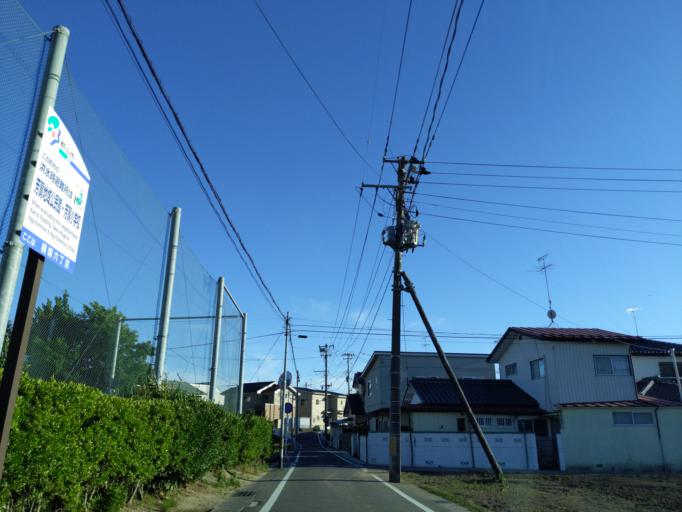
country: JP
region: Fukushima
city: Koriyama
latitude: 37.3912
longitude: 140.4059
